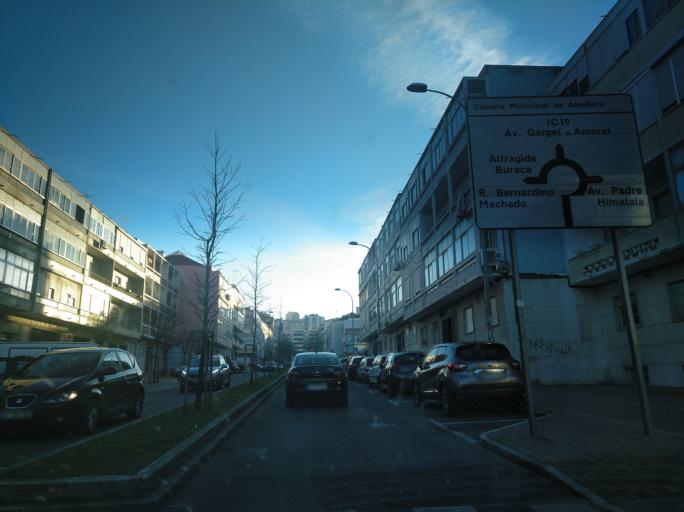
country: PT
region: Lisbon
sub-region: Amadora
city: Amadora
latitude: 38.7445
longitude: -9.2190
